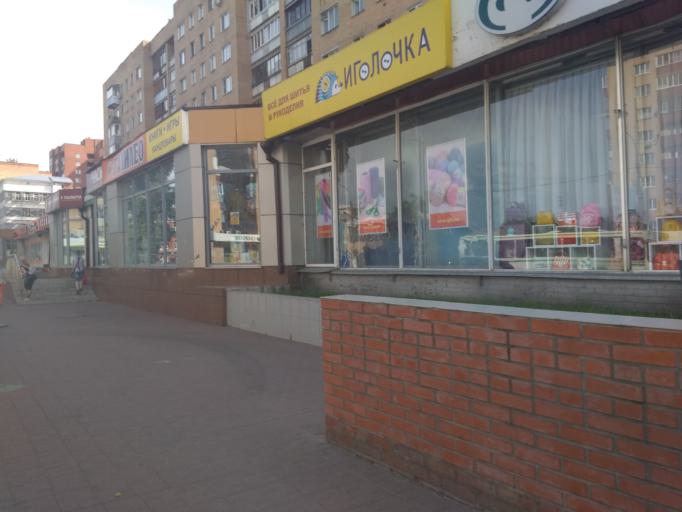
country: RU
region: Moskovskaya
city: Orekhovo-Zuyevo
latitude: 55.8017
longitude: 38.9758
